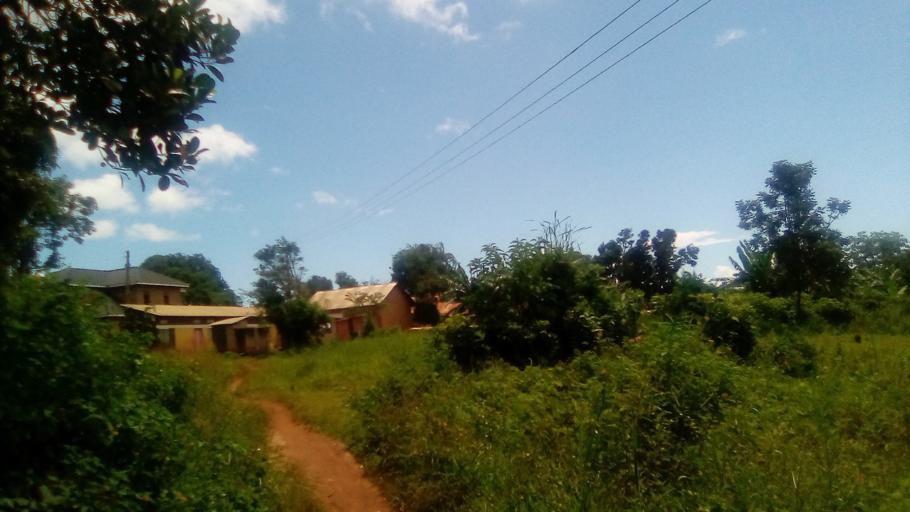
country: UG
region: Central Region
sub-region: Wakiso District
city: Entebbe
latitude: 0.1001
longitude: 32.5286
